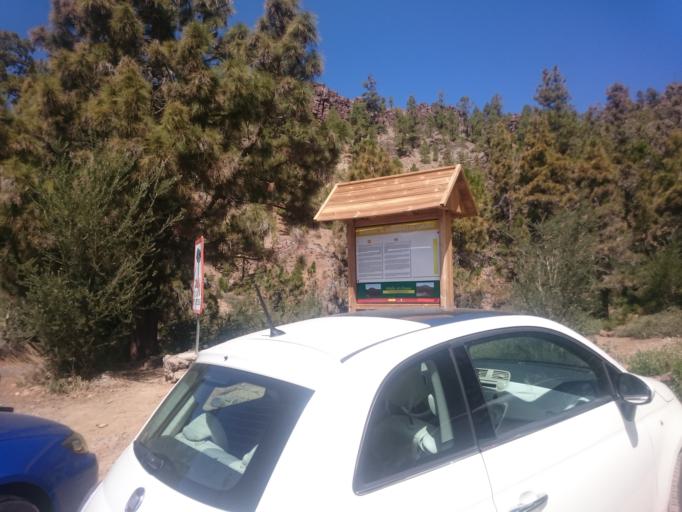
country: ES
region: Canary Islands
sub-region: Provincia de Santa Cruz de Tenerife
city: Vilaflor
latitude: 28.1889
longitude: -16.6569
